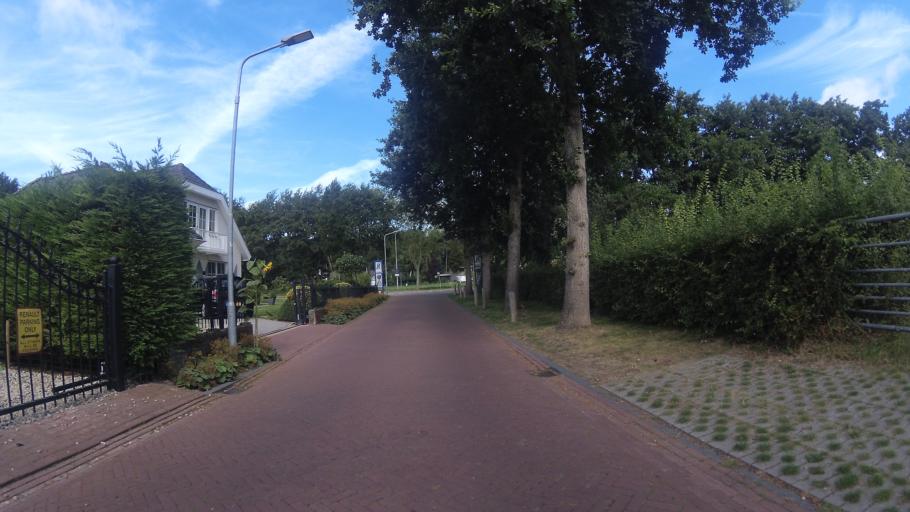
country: NL
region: Zeeland
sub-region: Schouwen-Duiveland
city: Burgh
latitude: 51.6747
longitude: 3.7084
